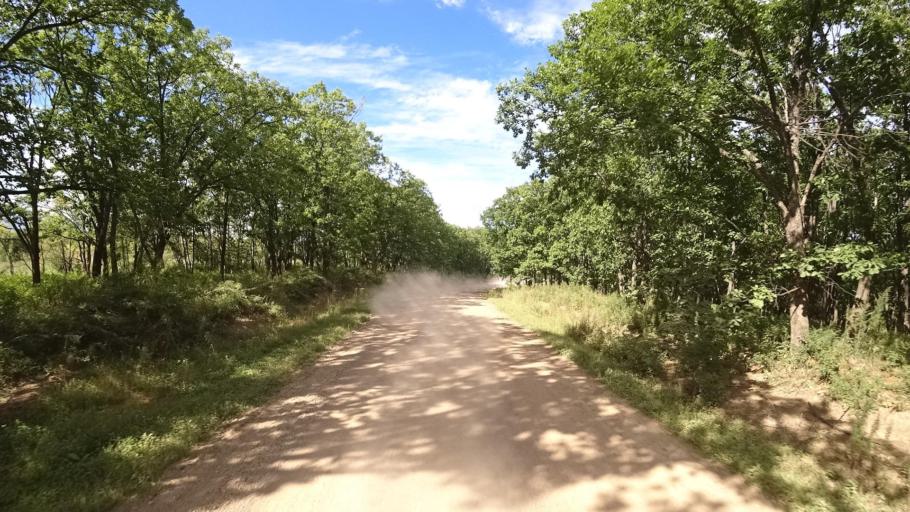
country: RU
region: Primorskiy
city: Yakovlevka
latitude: 44.4044
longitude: 133.5659
